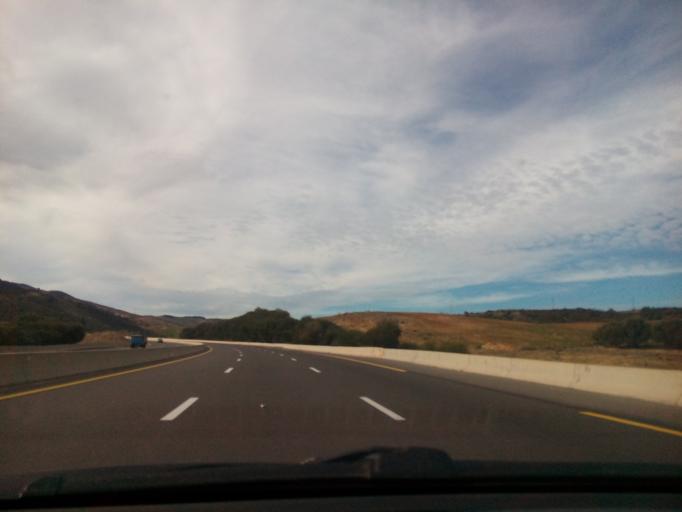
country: DZ
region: Sidi Bel Abbes
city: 'Ain el Berd
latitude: 35.4102
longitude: -0.4874
